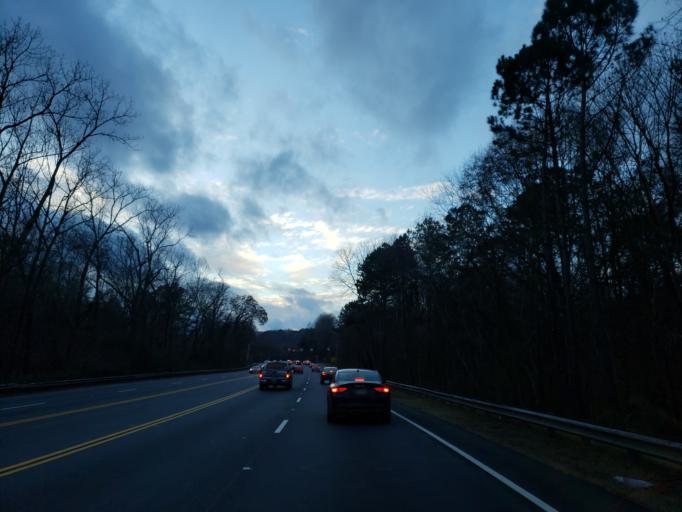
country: US
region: Georgia
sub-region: Fulton County
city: Union City
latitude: 33.6591
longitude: -84.5267
